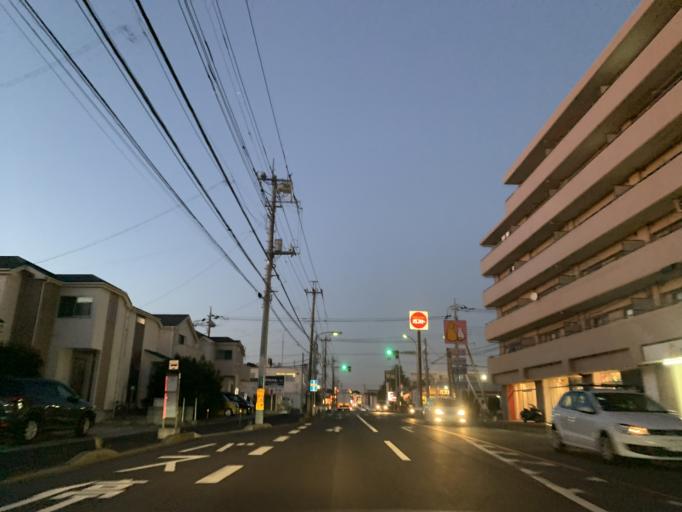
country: JP
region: Chiba
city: Nagareyama
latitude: 35.8910
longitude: 139.9009
